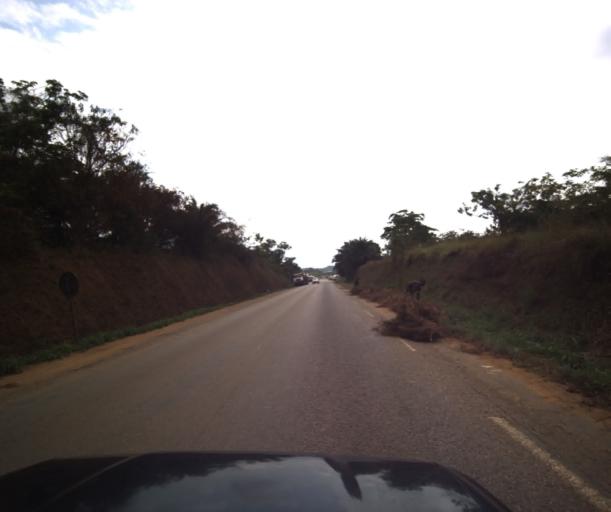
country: CM
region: Centre
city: Eseka
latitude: 3.8537
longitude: 10.5218
